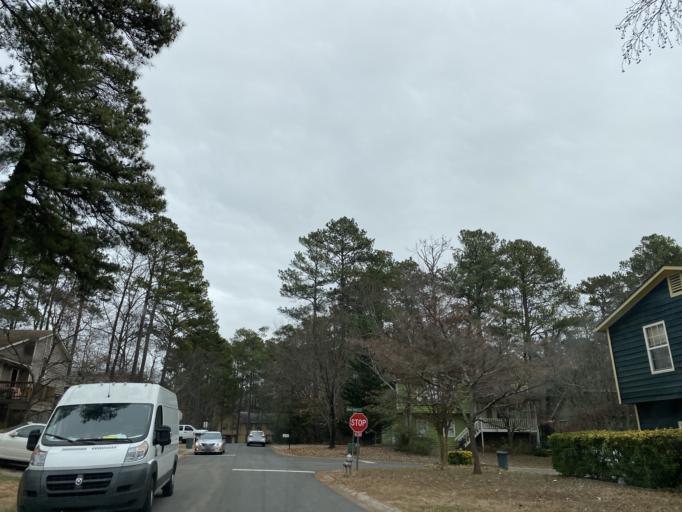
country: US
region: Georgia
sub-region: Cobb County
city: Fair Oaks
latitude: 33.9210
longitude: -84.5724
